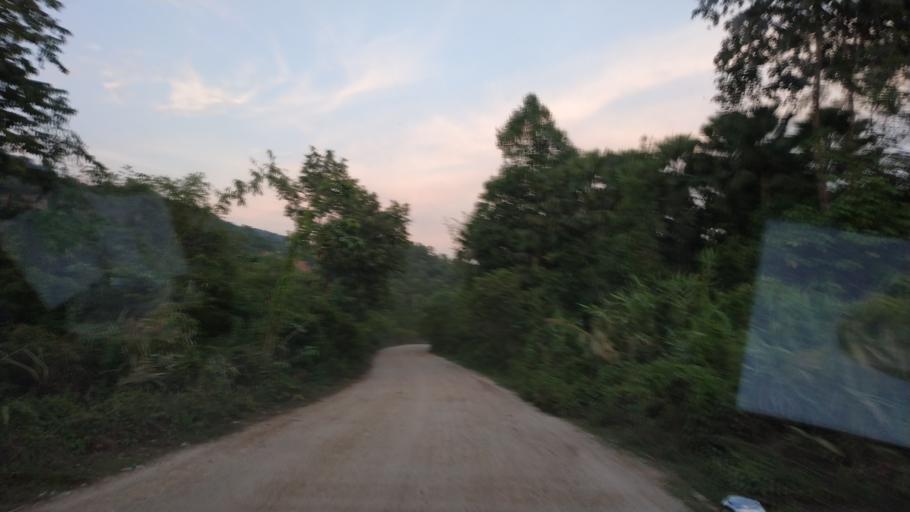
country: MM
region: Mon
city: Kyaikto
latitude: 17.4313
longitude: 97.0410
